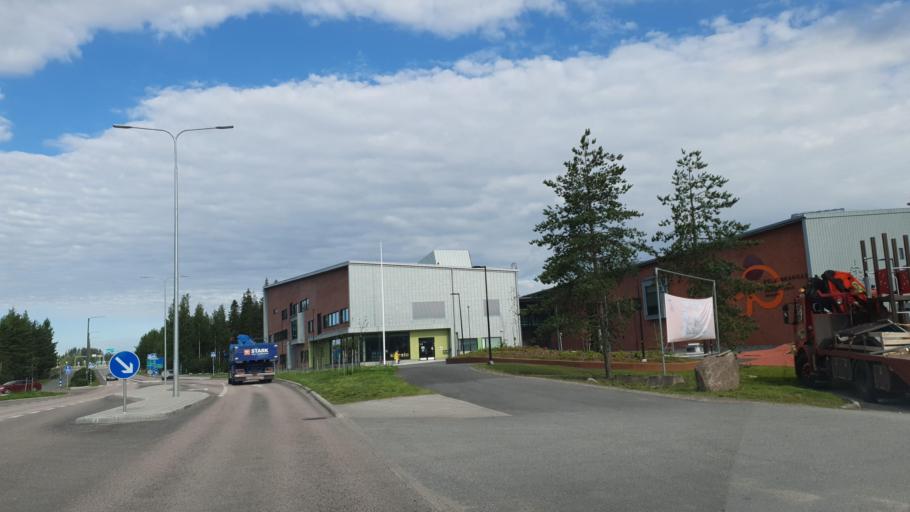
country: FI
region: Central Finland
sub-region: Jyvaeskylae
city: Jyvaeskylae
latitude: 62.1895
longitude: 25.7097
